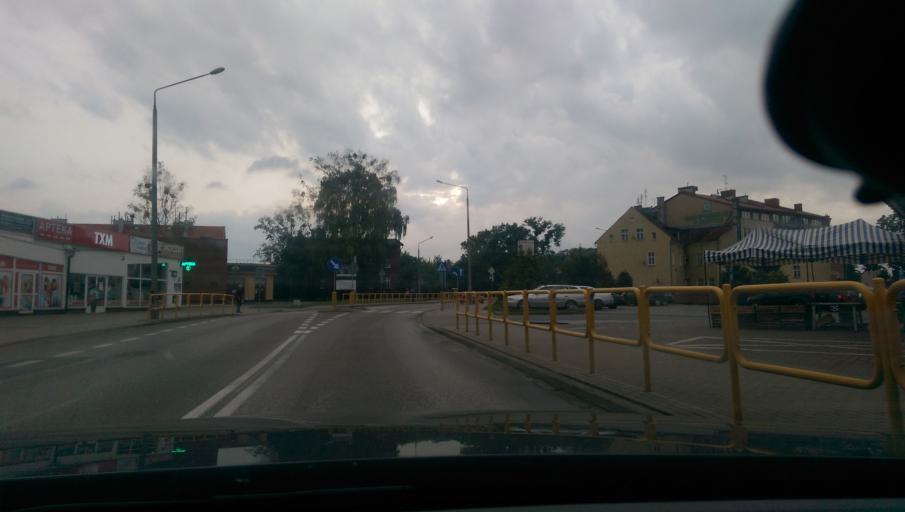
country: PL
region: Warmian-Masurian Voivodeship
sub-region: Powiat szczycienski
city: Szczytno
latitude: 53.5606
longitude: 21.0018
